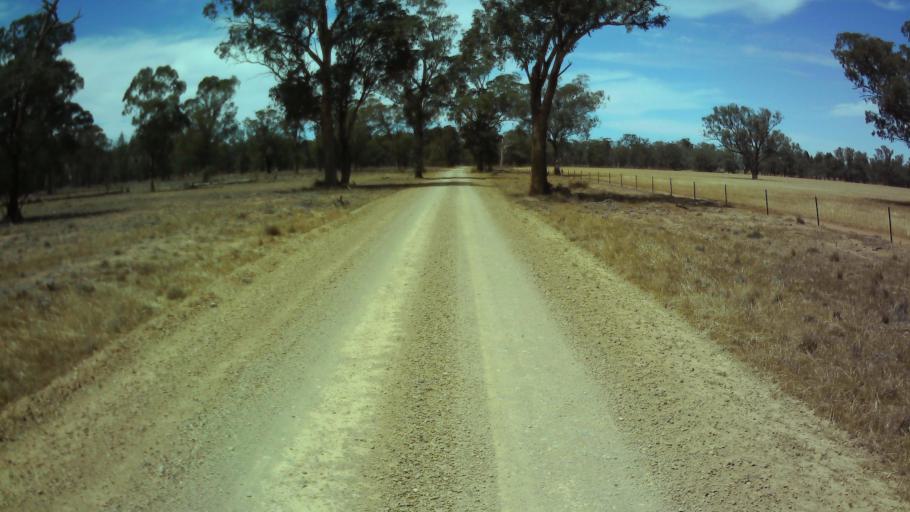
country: AU
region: New South Wales
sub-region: Weddin
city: Grenfell
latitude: -33.8529
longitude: 147.8058
